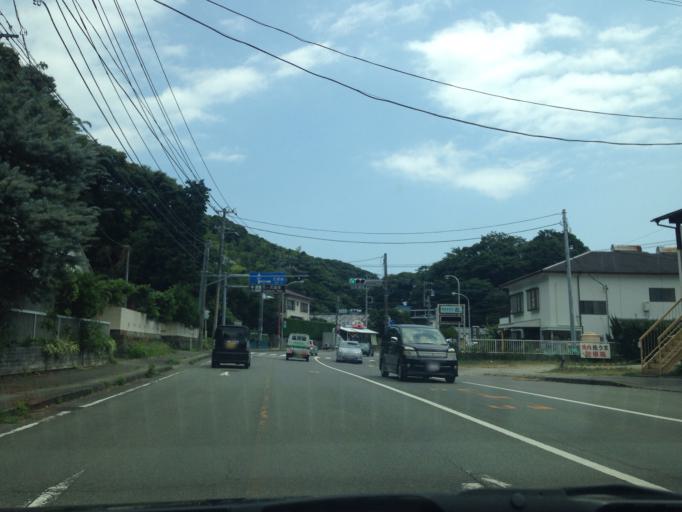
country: JP
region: Shizuoka
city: Shimoda
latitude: 34.6427
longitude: 138.8870
